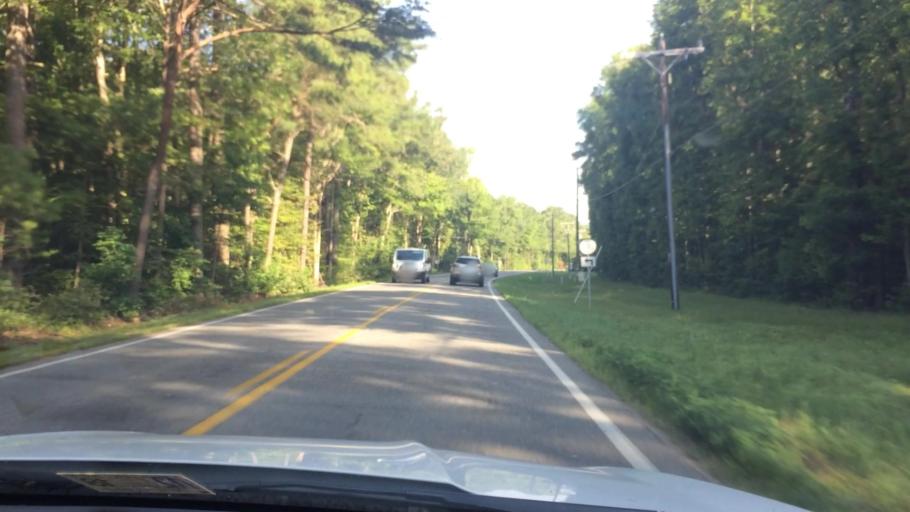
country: US
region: Virginia
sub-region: Middlesex County
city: Deltaville
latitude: 37.5435
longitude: -76.4370
